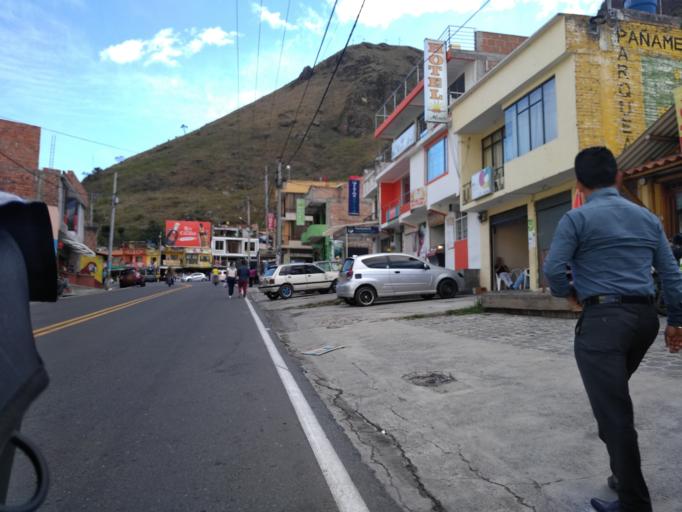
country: CO
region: Narino
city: Funes
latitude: 1.0505
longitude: -77.4526
